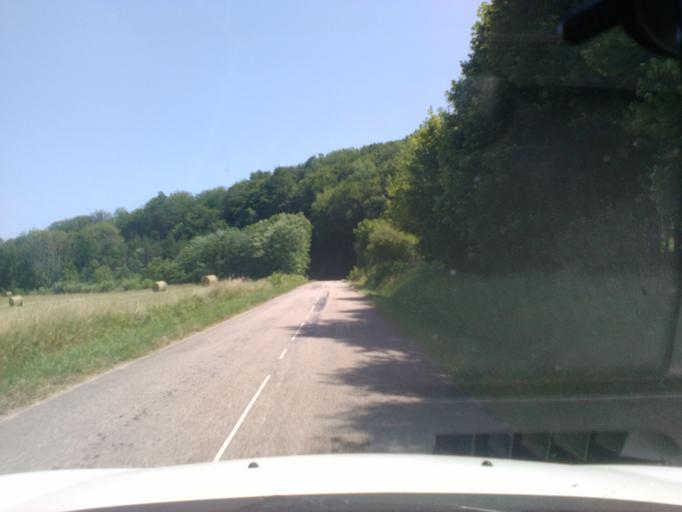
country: FR
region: Lorraine
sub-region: Departement des Vosges
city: Liffol-le-Grand
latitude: 48.3605
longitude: 5.6196
